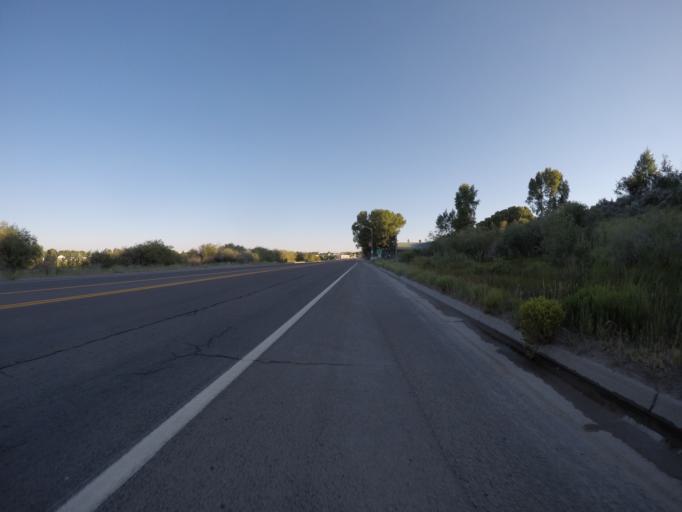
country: US
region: Wyoming
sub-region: Sublette County
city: Pinedale
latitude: 42.8626
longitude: -109.8525
